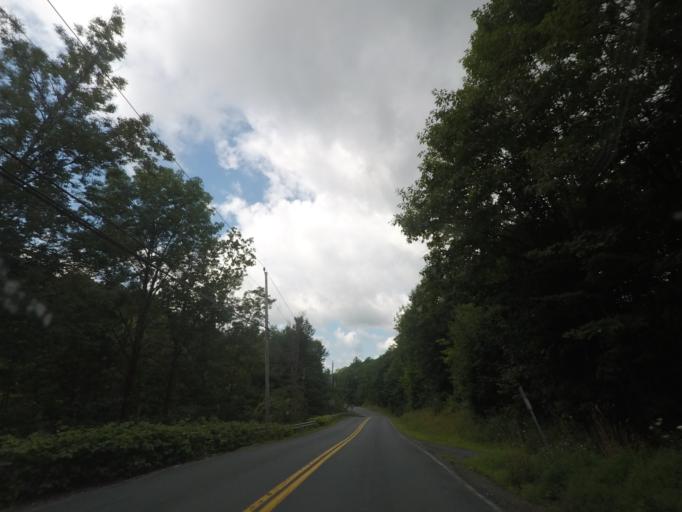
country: US
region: New York
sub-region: Rensselaer County
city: Averill Park
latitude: 42.6442
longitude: -73.5208
